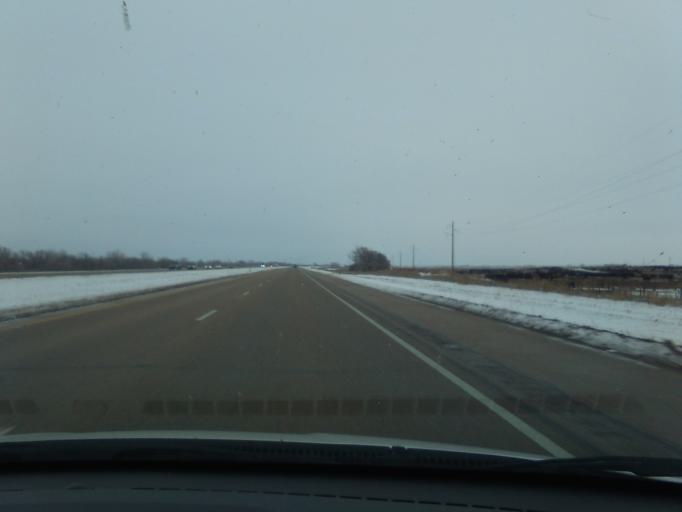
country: US
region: Nebraska
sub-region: Keith County
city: Ogallala
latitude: 41.0893
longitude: -101.8448
